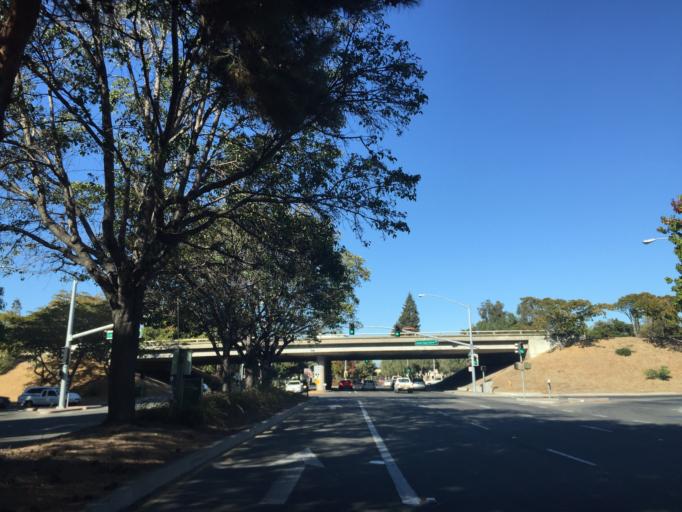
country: US
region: California
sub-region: Santa Clara County
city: Sunnyvale
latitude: 37.3775
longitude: -122.0132
